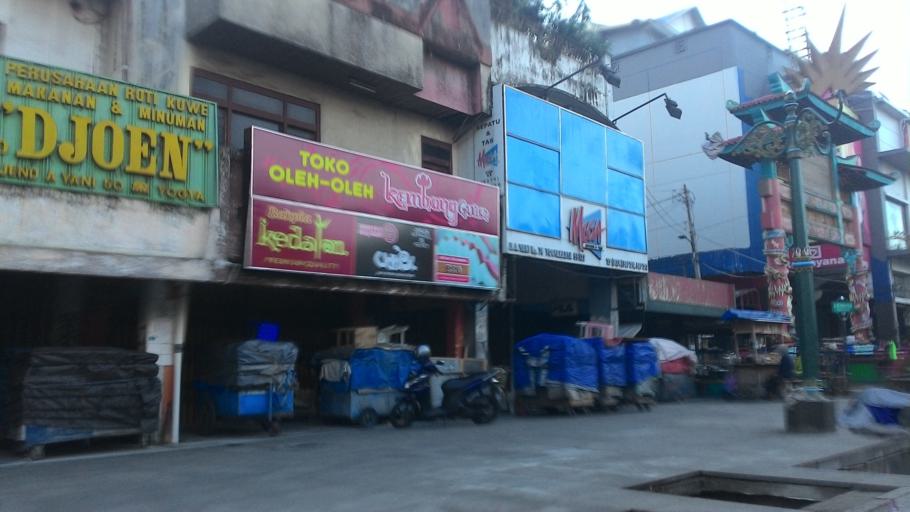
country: ID
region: Daerah Istimewa Yogyakarta
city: Yogyakarta
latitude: -7.7971
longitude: 110.3653
